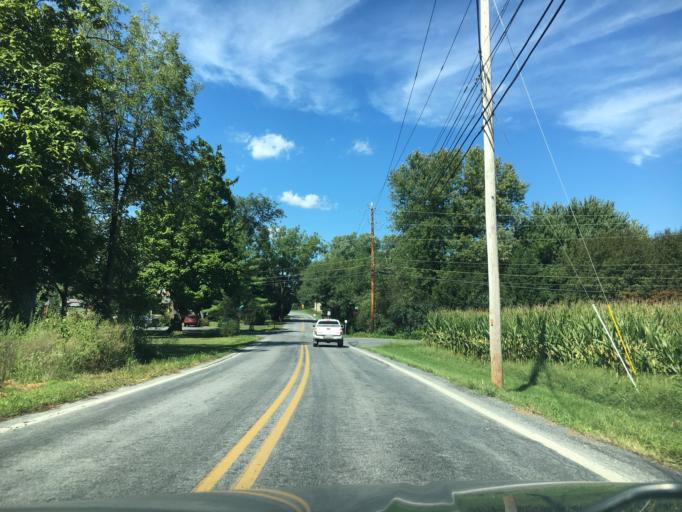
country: US
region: Pennsylvania
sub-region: Berks County
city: Topton
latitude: 40.5235
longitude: -75.6865
